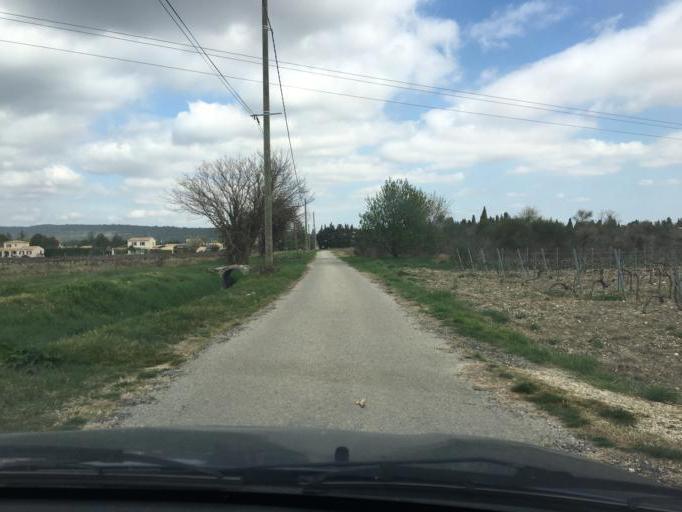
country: FR
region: Provence-Alpes-Cote d'Azur
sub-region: Departement du Vaucluse
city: Serignan-du-Comtat
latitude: 44.1796
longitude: 4.8339
